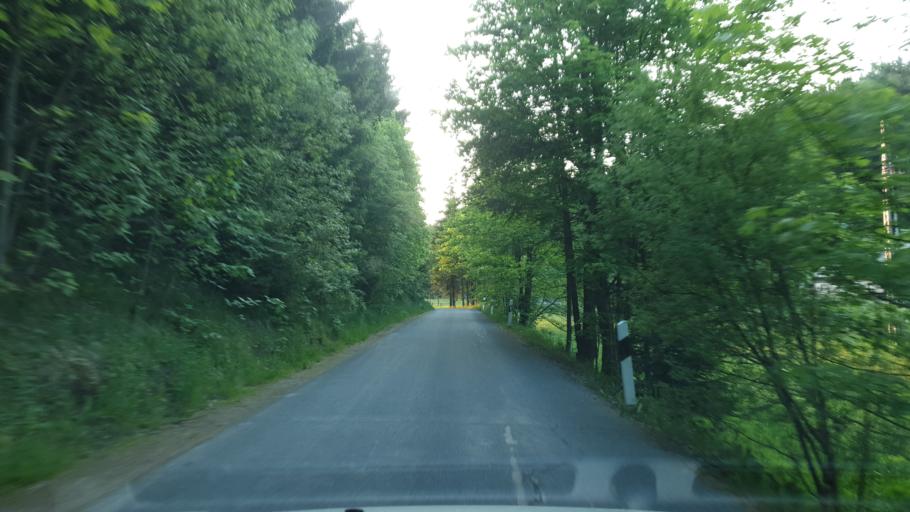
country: DE
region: Saxony
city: Klingenthal
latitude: 50.3837
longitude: 12.4565
